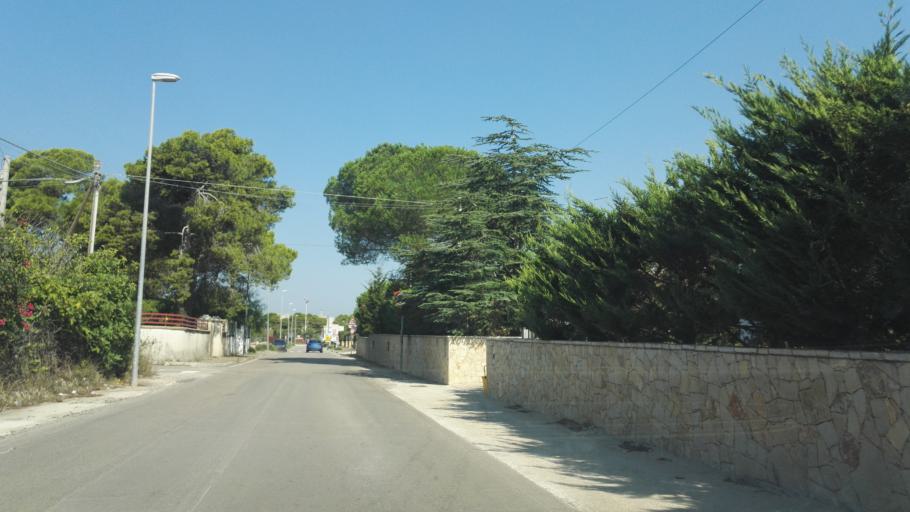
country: IT
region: Apulia
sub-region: Provincia di Lecce
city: Nardo
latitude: 40.1474
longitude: 18.0030
